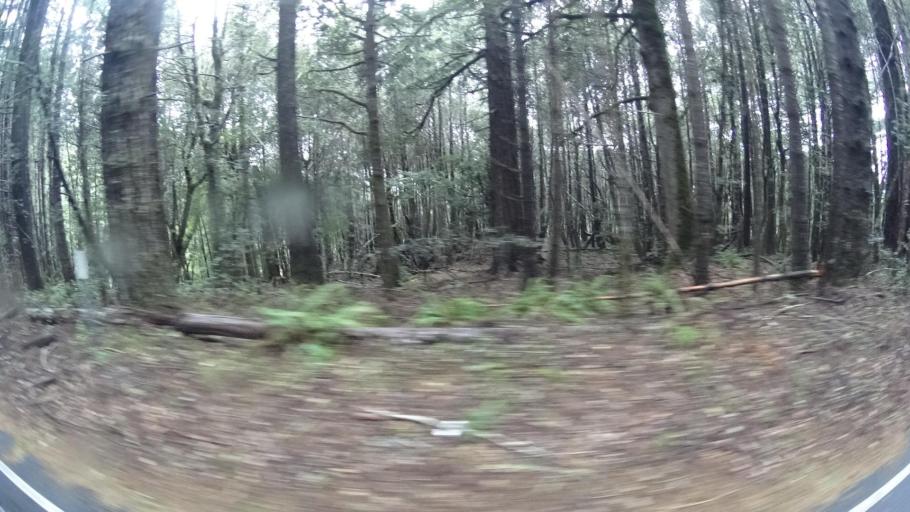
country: US
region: California
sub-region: Humboldt County
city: Westhaven-Moonstone
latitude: 41.2185
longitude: -123.9578
